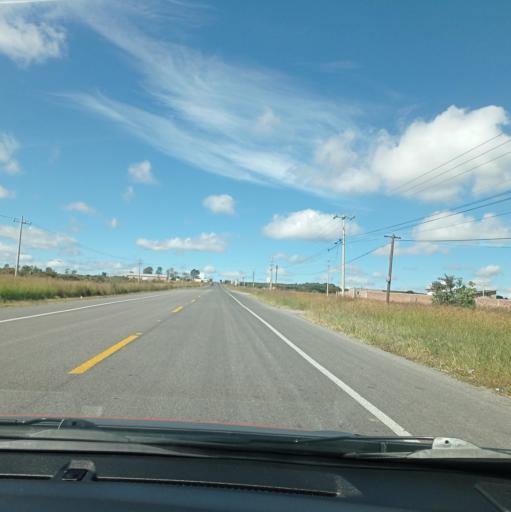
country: MX
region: Jalisco
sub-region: San Julian
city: Colonia Veintitres de Mayo
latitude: 21.0121
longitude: -102.2056
